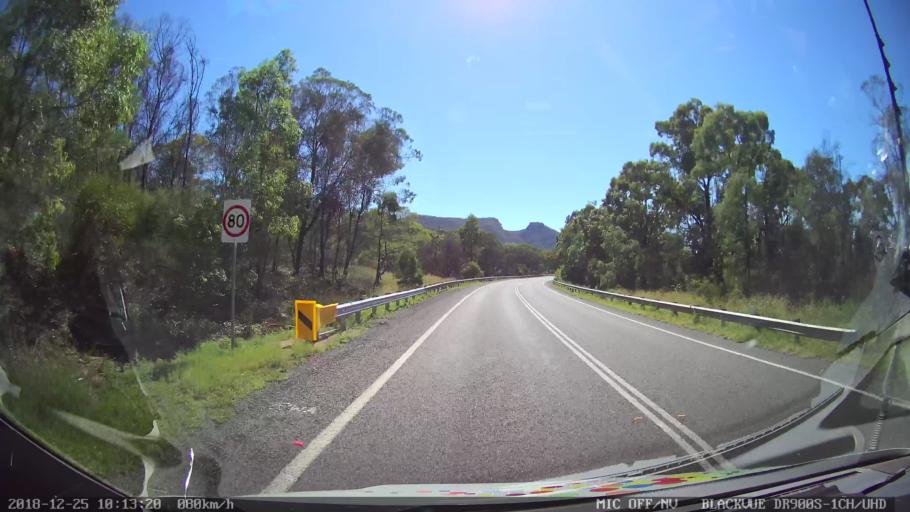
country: AU
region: New South Wales
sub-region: Muswellbrook
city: Denman
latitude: -32.3253
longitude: 150.5430
